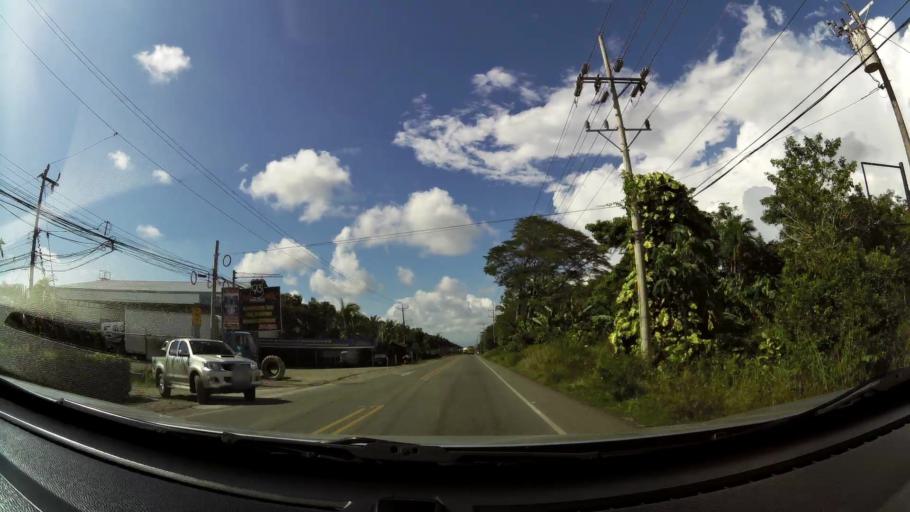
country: CR
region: Puntarenas
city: Quepos
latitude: 9.4653
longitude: -84.1856
